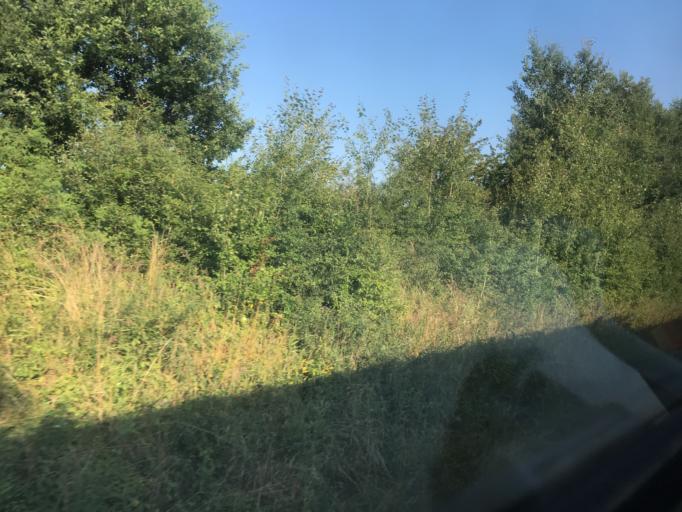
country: CZ
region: Jihocesky
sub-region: Okres Jindrichuv Hradec
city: Trebon
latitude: 49.0214
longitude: 14.7574
